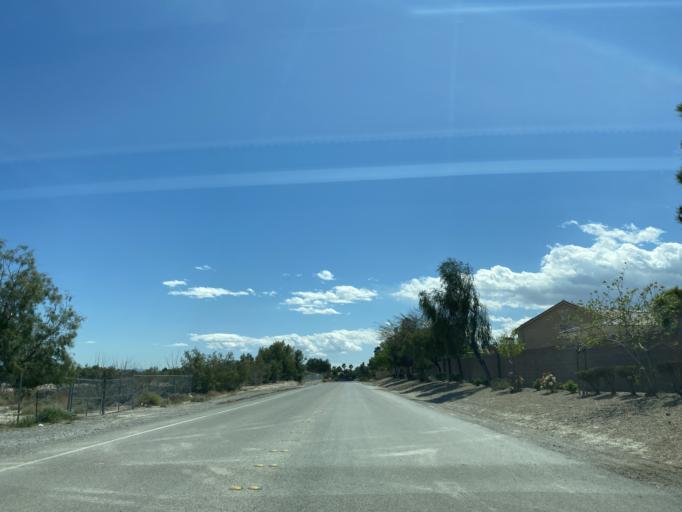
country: US
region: Nevada
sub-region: Clark County
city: North Las Vegas
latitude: 36.3121
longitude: -115.2378
